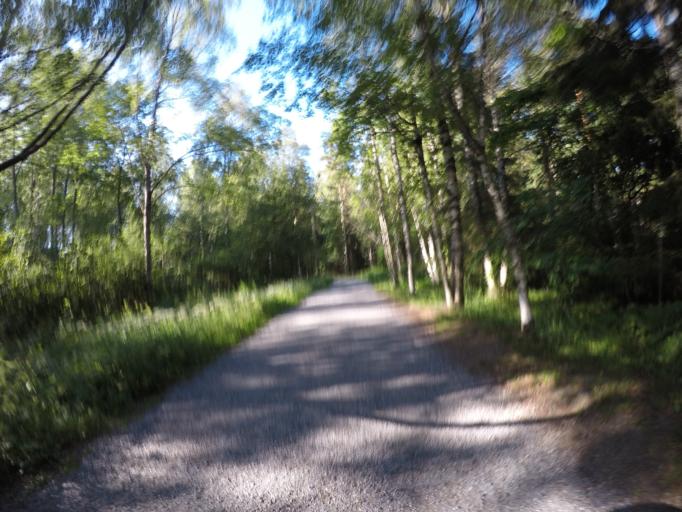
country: FI
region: Haeme
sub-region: Haemeenlinna
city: Haemeenlinna
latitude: 61.0181
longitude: 24.4902
